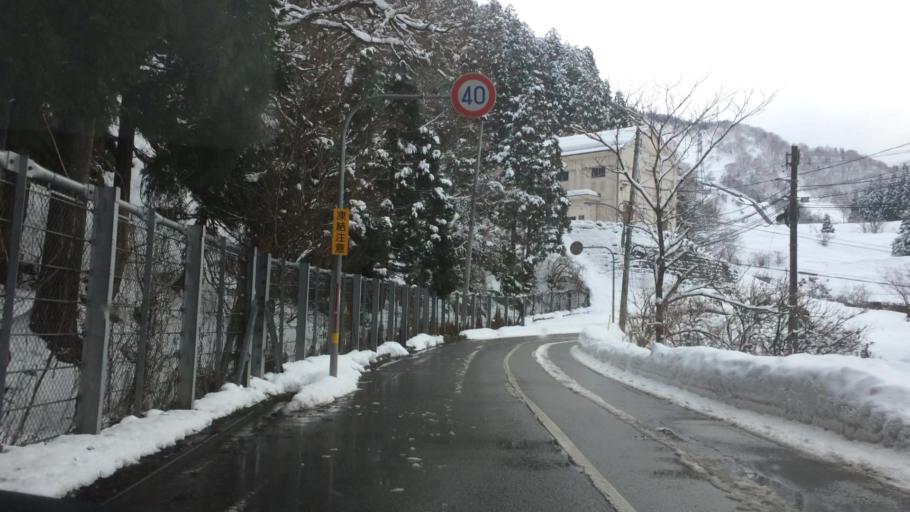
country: JP
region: Toyama
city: Kamiichi
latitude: 36.5689
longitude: 137.3656
